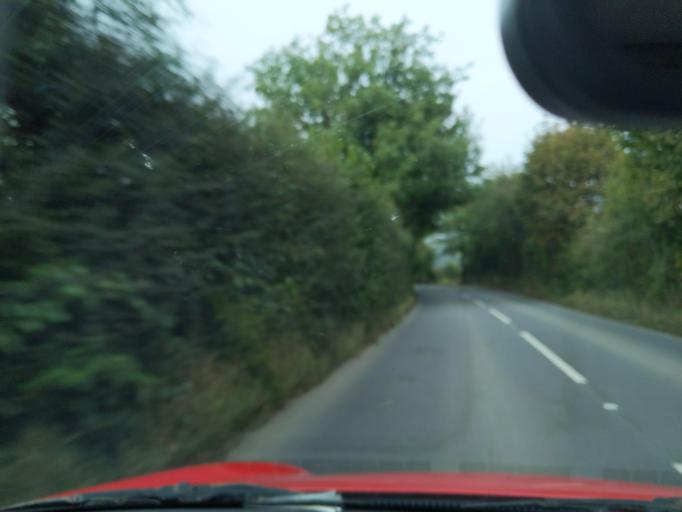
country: GB
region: England
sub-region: Devon
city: Great Torrington
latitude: 50.9348
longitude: -4.1497
